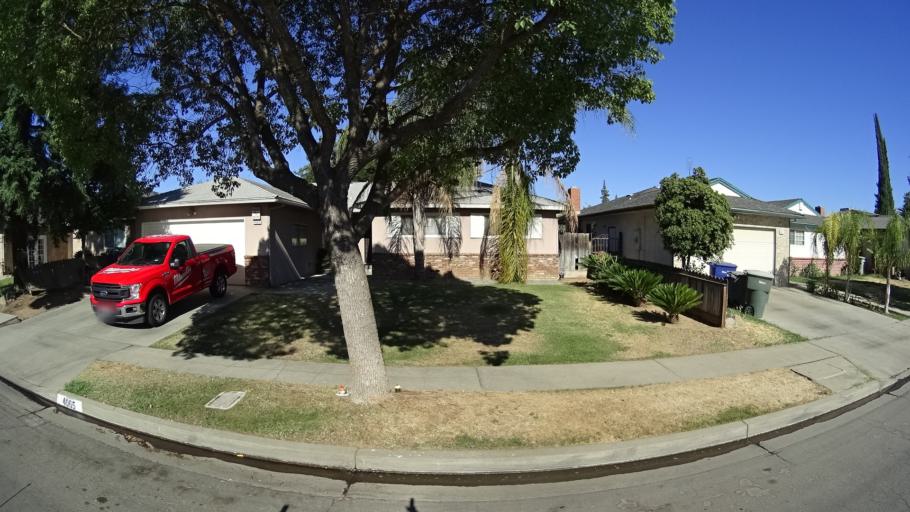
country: US
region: California
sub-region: Fresno County
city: Fresno
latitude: 36.7915
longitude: -119.8403
